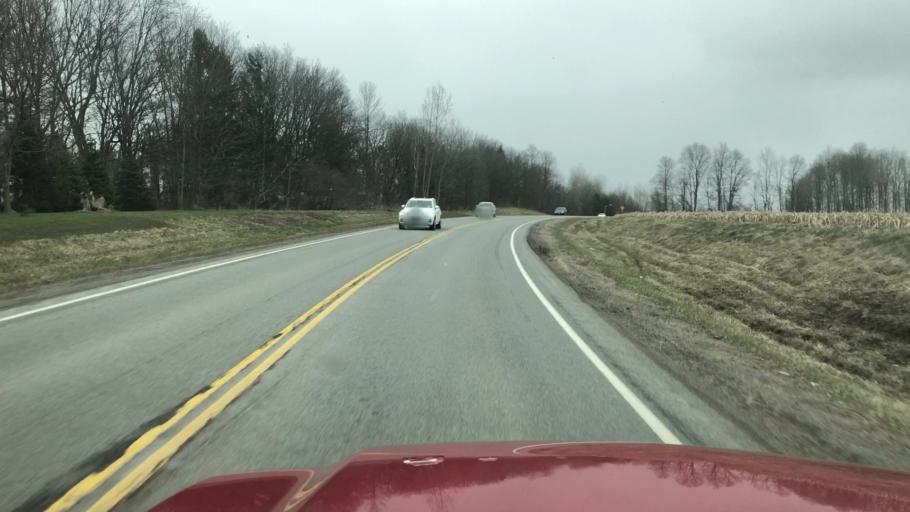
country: US
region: New York
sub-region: Monroe County
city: Fairport
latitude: 43.1305
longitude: -77.3651
